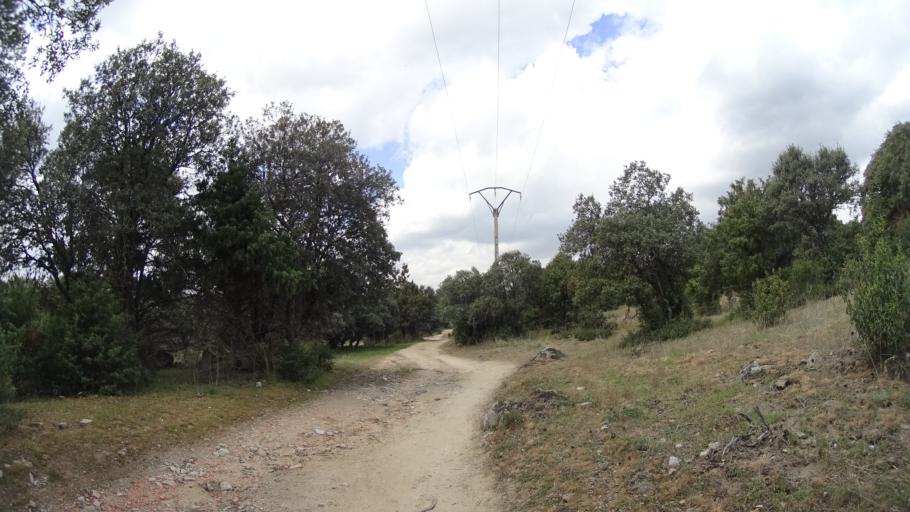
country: ES
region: Madrid
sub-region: Provincia de Madrid
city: Hoyo de Manzanares
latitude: 40.6178
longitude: -3.8952
